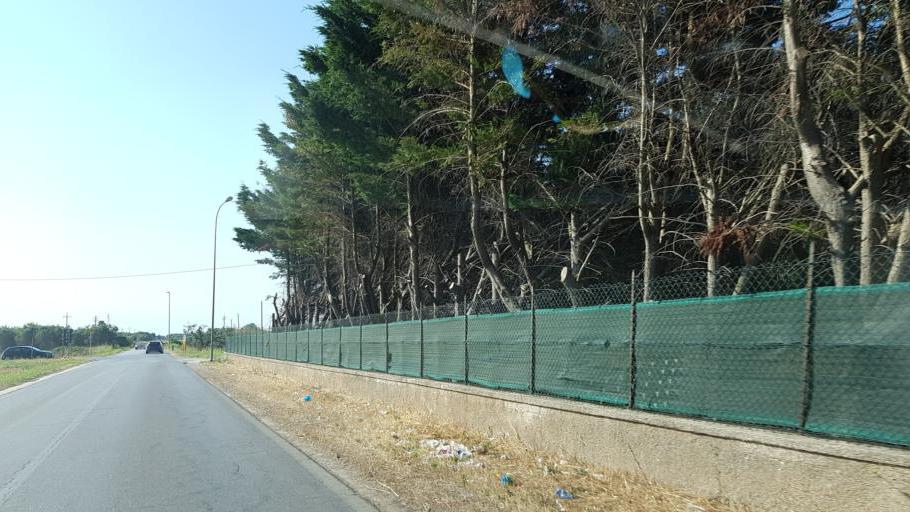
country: IT
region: Apulia
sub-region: Provincia di Brindisi
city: Mesagne
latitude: 40.5452
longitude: 17.8221
